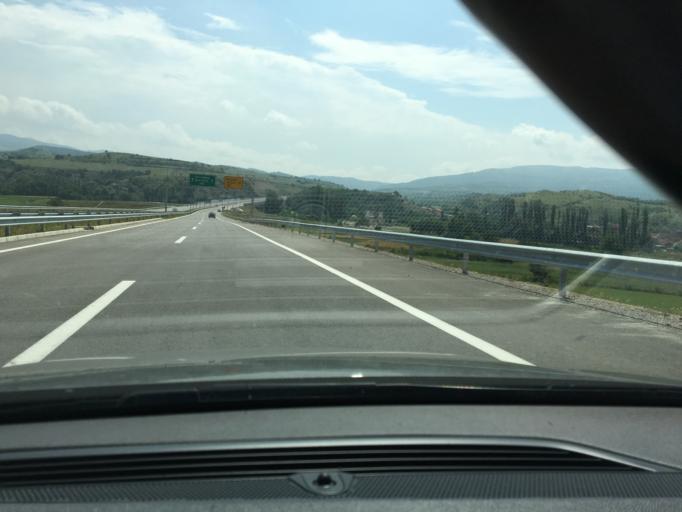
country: MK
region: Petrovec
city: Sredno Konjare
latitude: 41.9626
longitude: 21.7086
